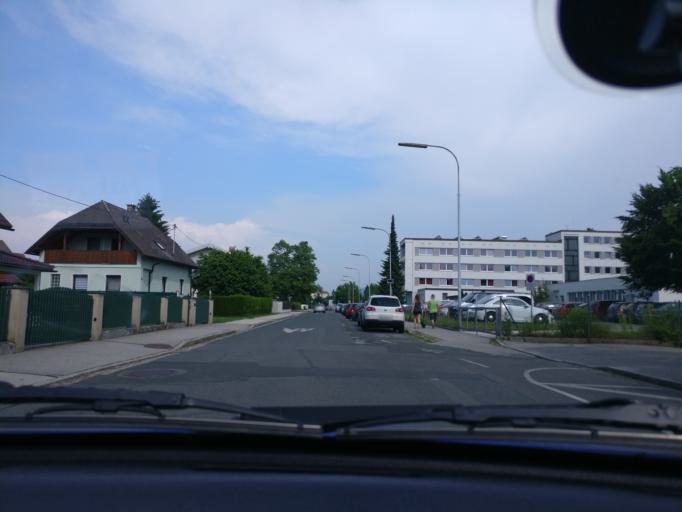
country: AT
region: Carinthia
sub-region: Klagenfurt am Woerthersee
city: Klagenfurt am Woerthersee
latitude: 46.6092
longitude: 14.2855
